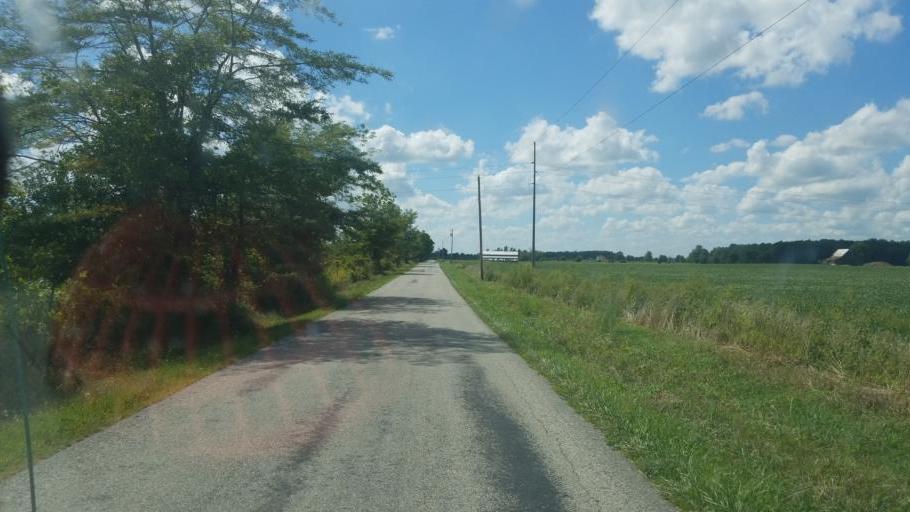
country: US
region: Ohio
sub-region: Marion County
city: Prospect
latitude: 40.3726
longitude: -83.2175
